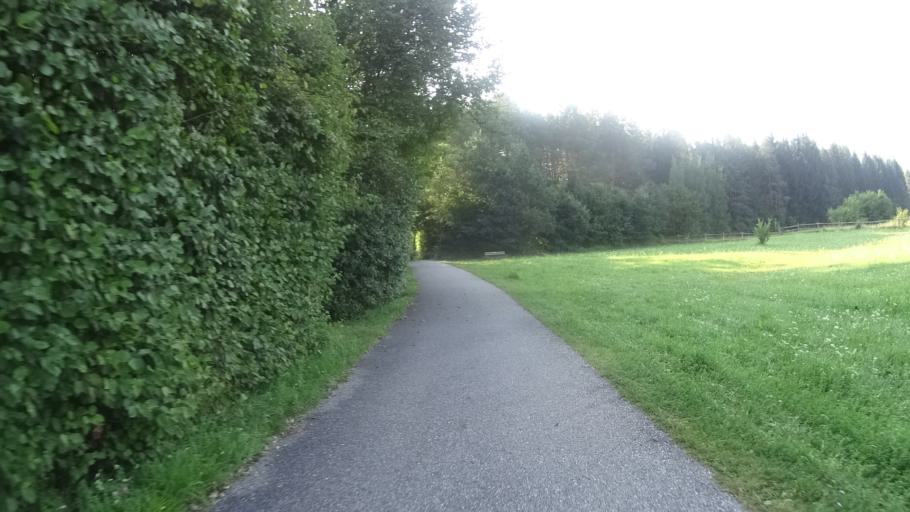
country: AT
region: Carinthia
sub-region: Politischer Bezirk Klagenfurt Land
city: Ludmannsdorf
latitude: 46.5349
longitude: 14.1148
